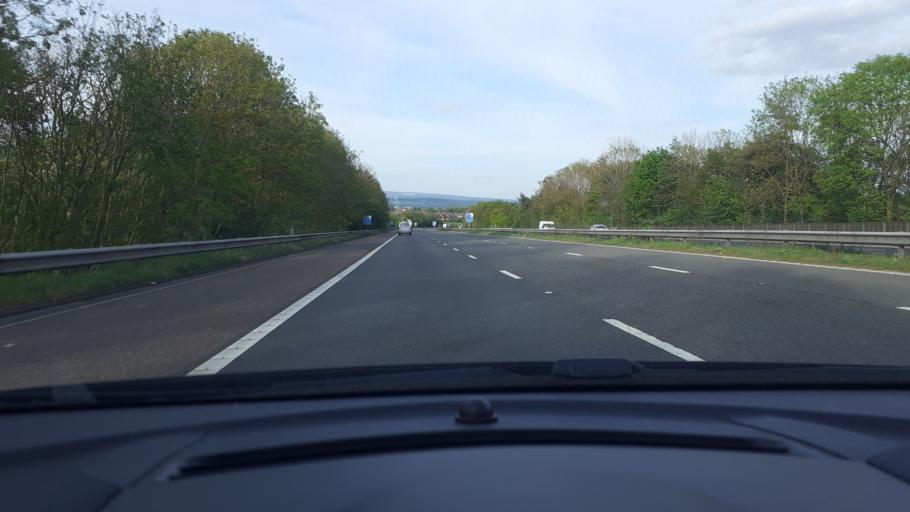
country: GB
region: England
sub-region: St. Helens
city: Billinge
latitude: 53.5337
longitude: -2.7226
